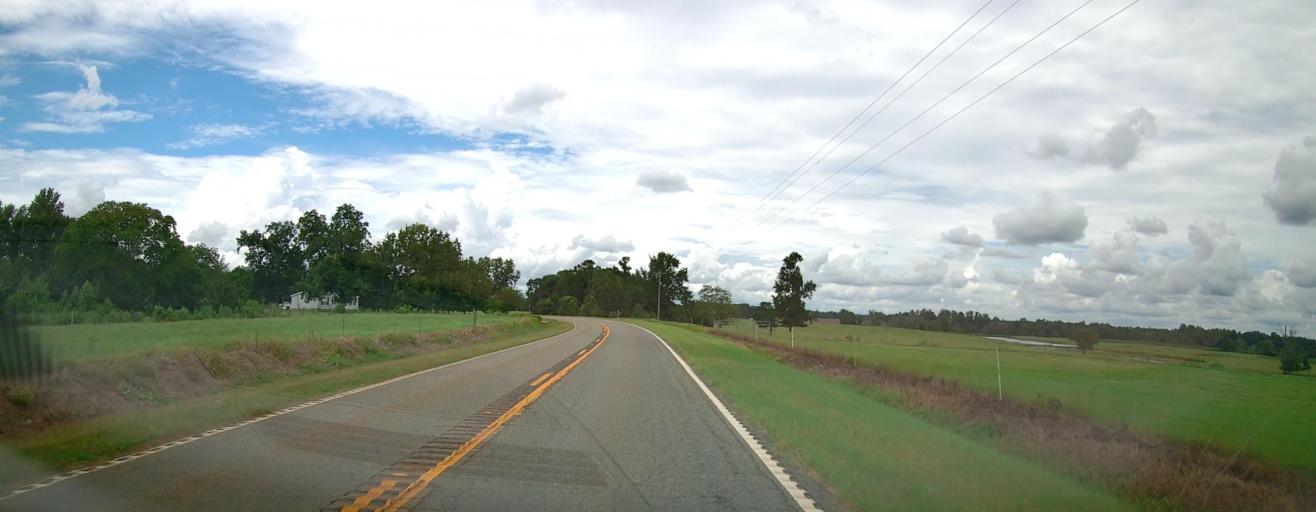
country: US
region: Georgia
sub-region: Dooly County
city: Unadilla
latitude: 32.2730
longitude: -83.8156
